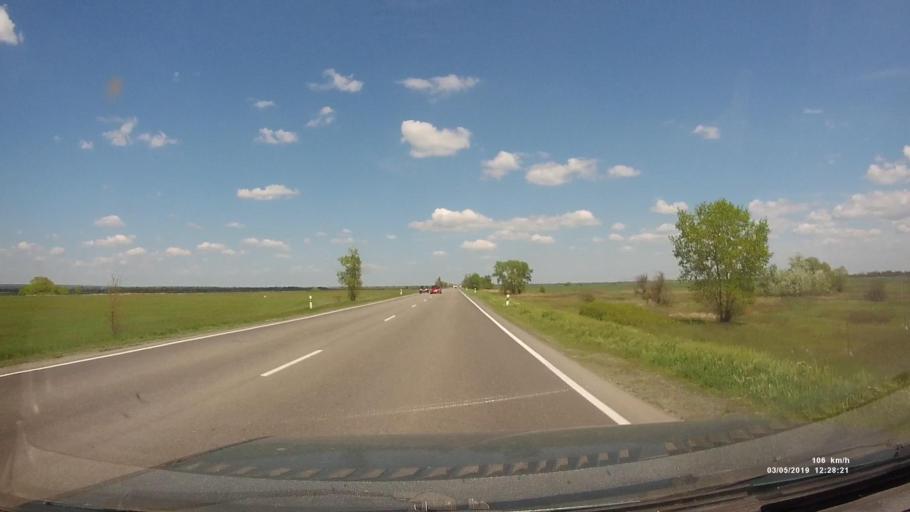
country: RU
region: Rostov
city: Semikarakorsk
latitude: 47.4717
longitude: 40.7279
